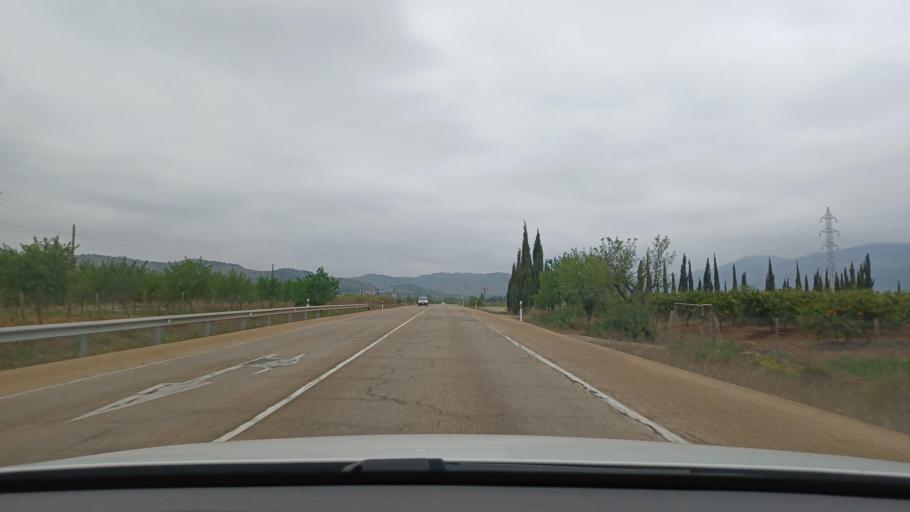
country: ES
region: Valencia
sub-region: Provincia de Castello
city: Torreblanca
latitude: 40.2468
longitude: 0.2329
